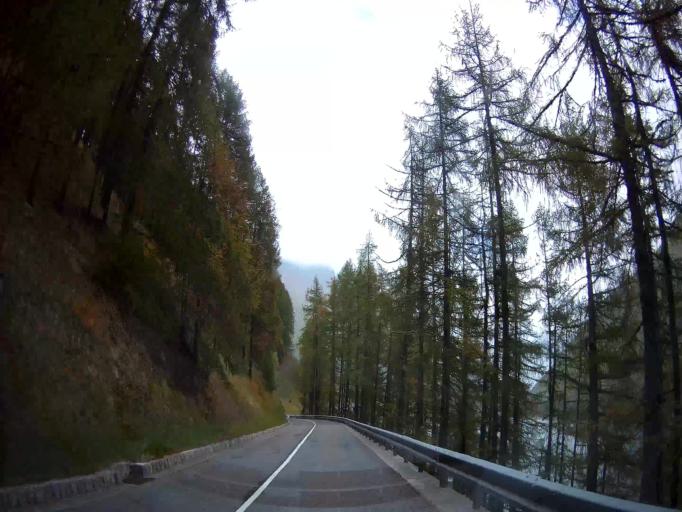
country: IT
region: Trentino-Alto Adige
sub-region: Bolzano
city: Senales
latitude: 46.7384
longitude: 10.8321
